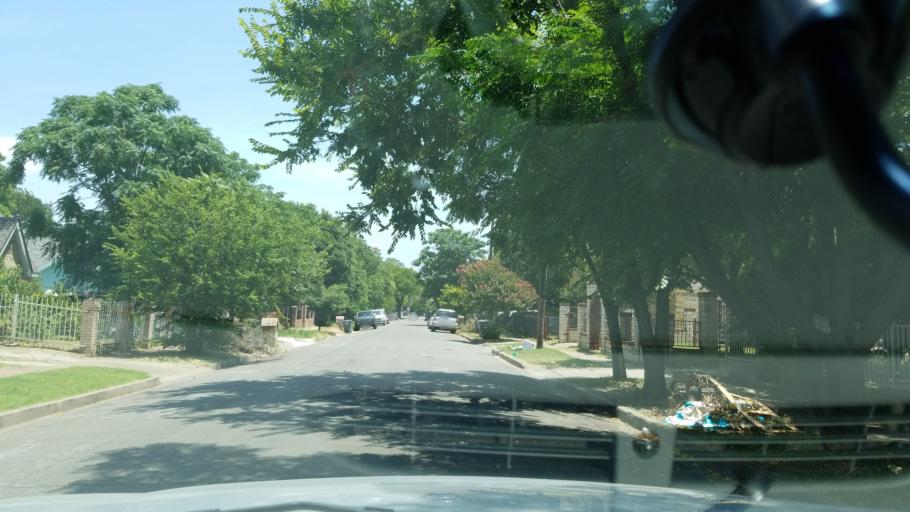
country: US
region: Texas
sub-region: Dallas County
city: Cockrell Hill
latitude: 32.7282
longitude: -96.8659
